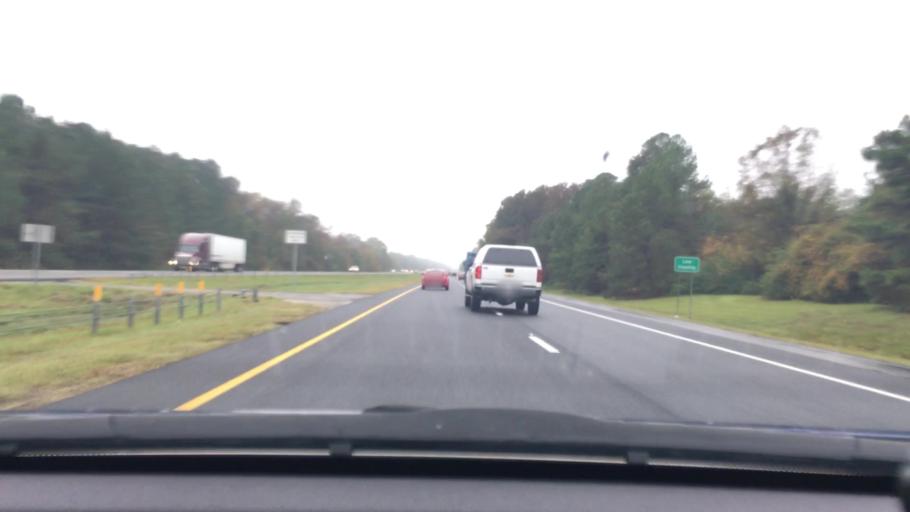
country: US
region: South Carolina
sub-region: Lee County
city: Bishopville
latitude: 34.1973
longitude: -80.1052
